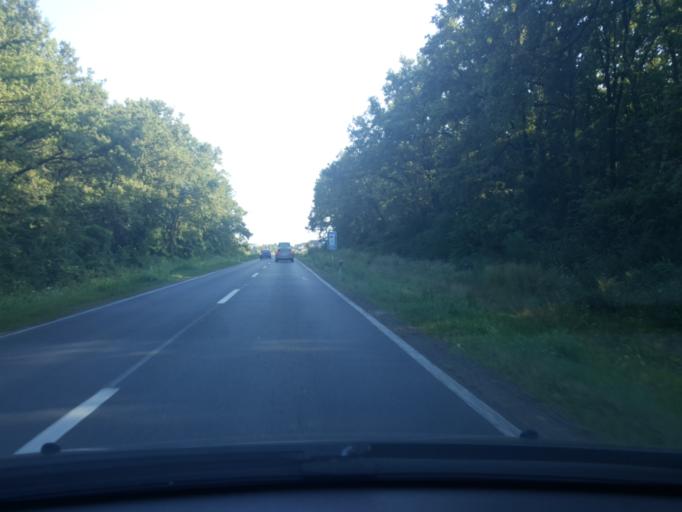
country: RS
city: Hrtkovci
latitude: 44.8957
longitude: 19.7641
